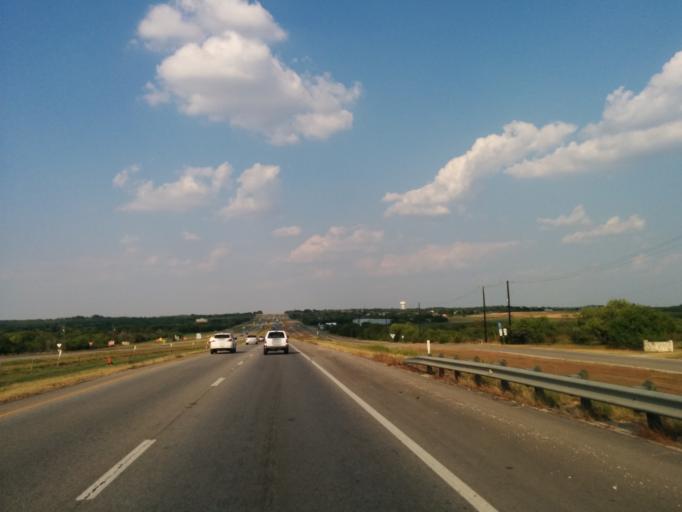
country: US
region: Texas
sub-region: Bexar County
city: Converse
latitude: 29.4776
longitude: -98.2535
